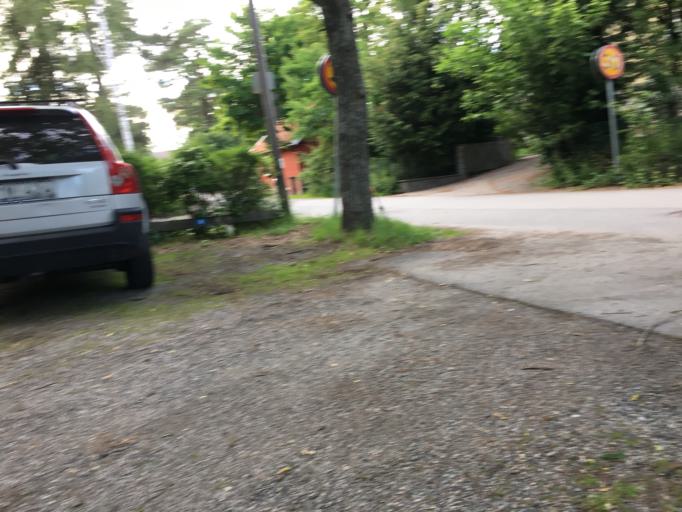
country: SE
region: Stockholm
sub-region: Nacka Kommun
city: Fisksatra
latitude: 59.3172
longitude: 18.2383
